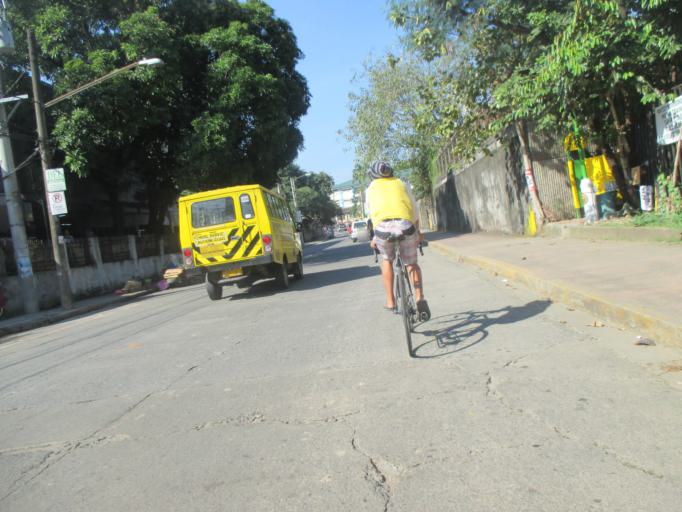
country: PH
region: Metro Manila
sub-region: Marikina
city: Calumpang
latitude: 14.6337
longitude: 121.0838
